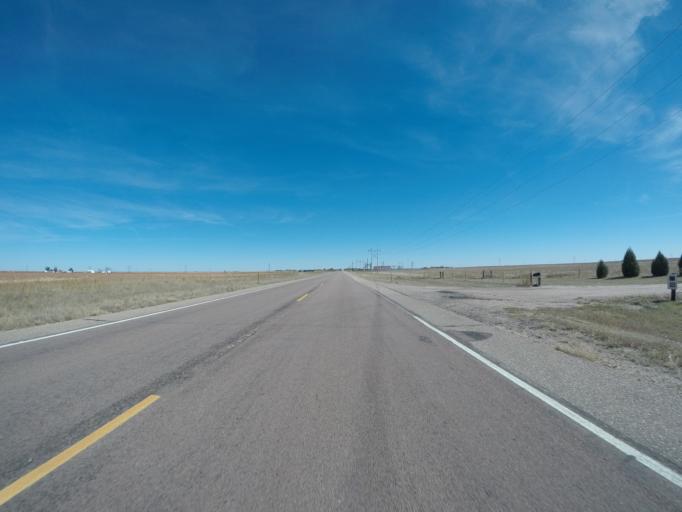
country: US
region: Colorado
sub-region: Yuma County
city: Yuma
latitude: 39.6559
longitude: -102.7131
